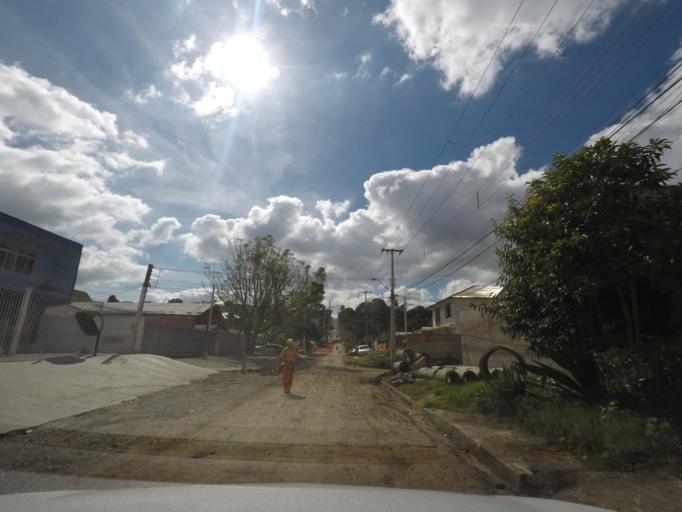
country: BR
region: Parana
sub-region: Sao Jose Dos Pinhais
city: Sao Jose dos Pinhais
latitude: -25.4882
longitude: -49.2317
